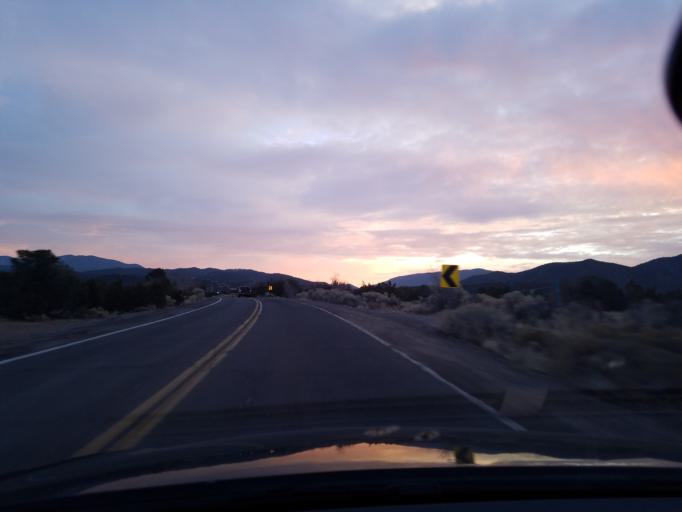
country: US
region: New Mexico
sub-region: Santa Fe County
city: Santa Fe
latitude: 35.6915
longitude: -105.9277
